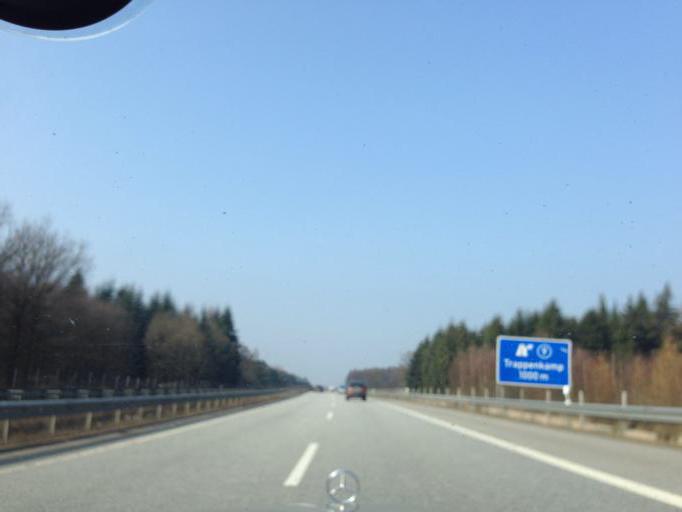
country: DE
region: Schleswig-Holstein
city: Daldorf
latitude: 54.0286
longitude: 10.2451
